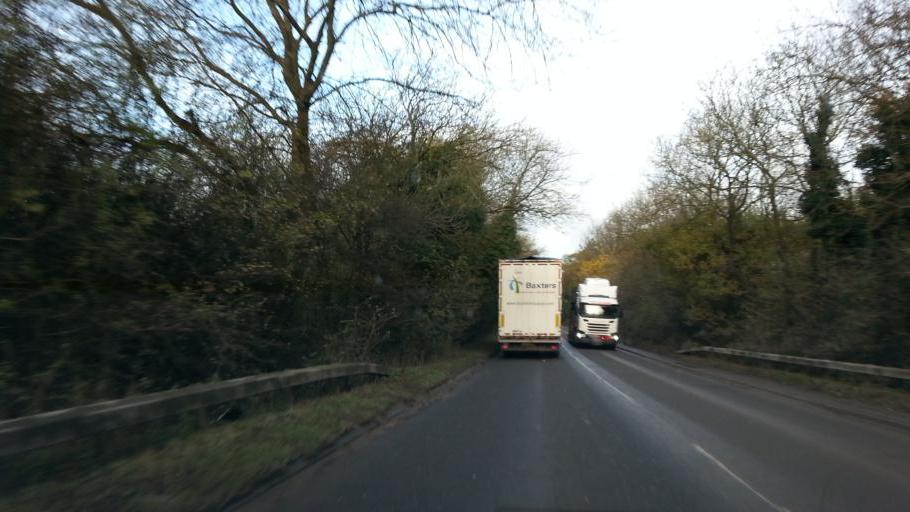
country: GB
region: England
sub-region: Leicestershire
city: Coalville
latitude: 52.7064
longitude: -1.3296
